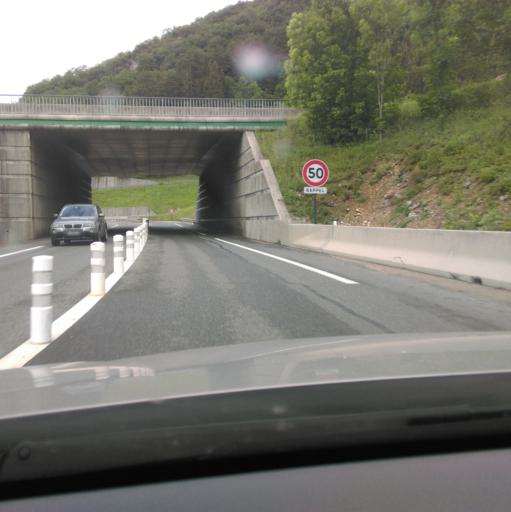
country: FR
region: Rhone-Alpes
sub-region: Departement de l'Ain
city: Montreal-la-Cluse
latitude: 46.1794
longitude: 5.5617
